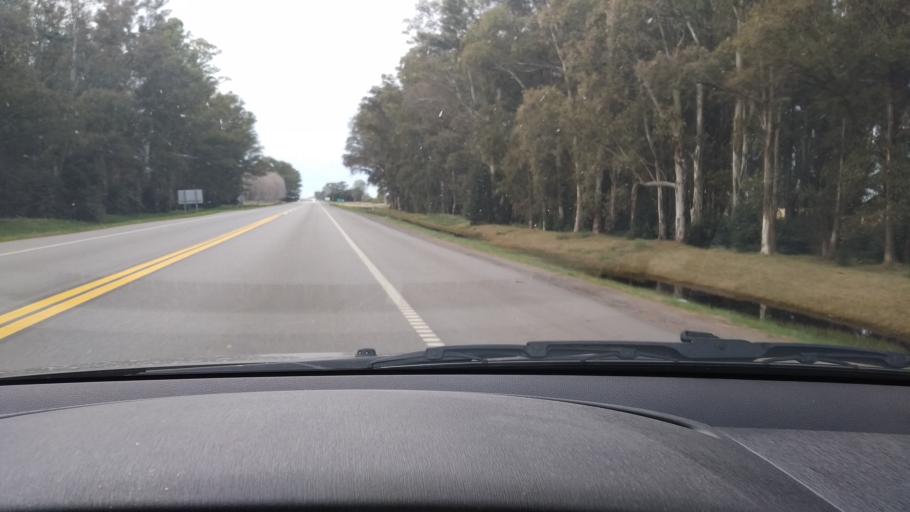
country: AR
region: Buenos Aires
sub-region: Partido de Las Flores
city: Las Flores
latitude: -36.3845
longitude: -59.4887
